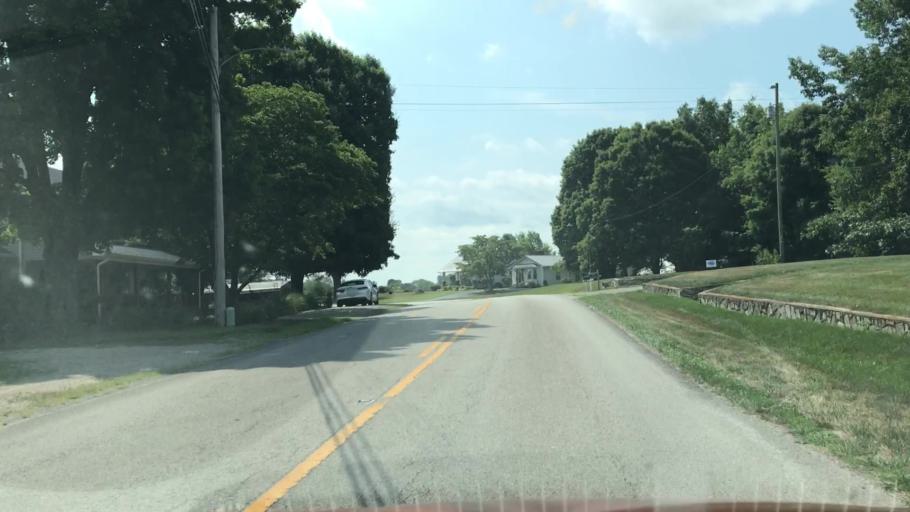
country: US
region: Kentucky
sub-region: Barren County
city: Glasgow
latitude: 36.8909
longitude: -85.8545
